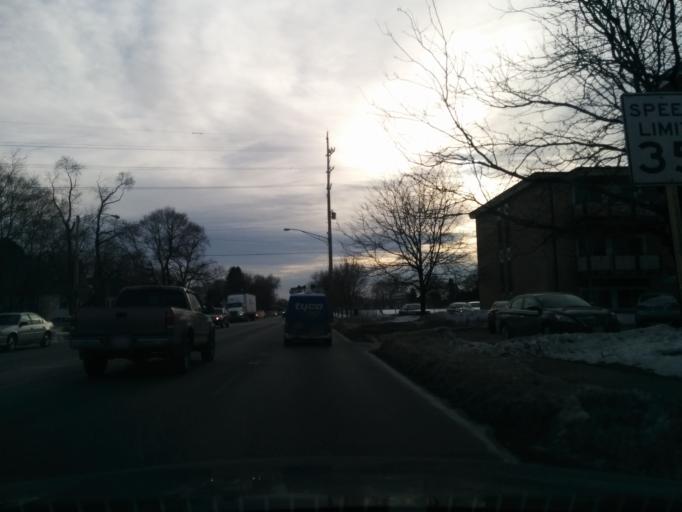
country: US
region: Illinois
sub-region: Cook County
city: Schiller Park
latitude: 41.9562
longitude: -87.8766
